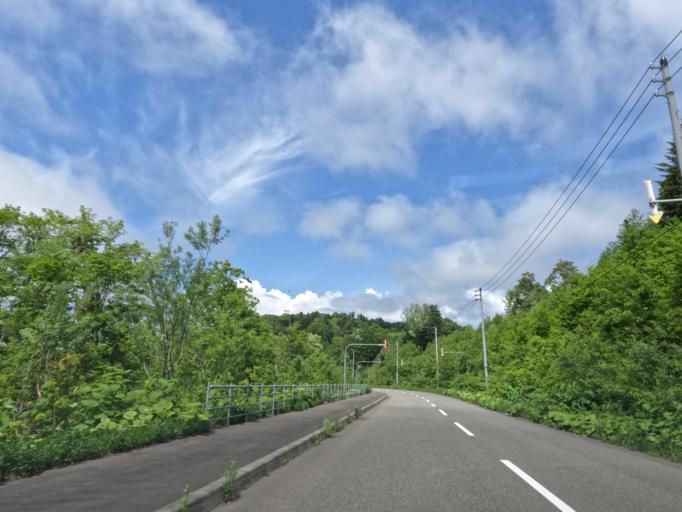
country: JP
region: Hokkaido
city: Tobetsu
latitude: 43.3532
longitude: 141.5693
